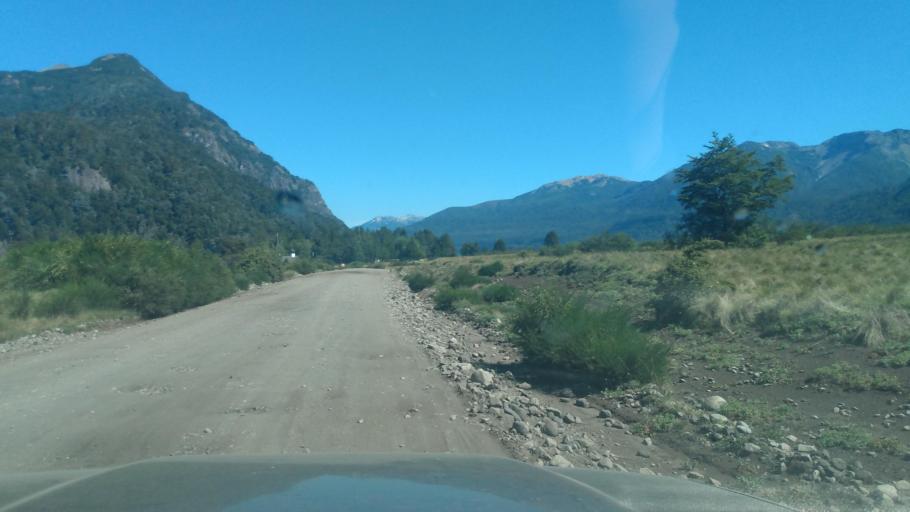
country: AR
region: Neuquen
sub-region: Departamento de Lacar
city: San Martin de los Andes
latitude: -39.7455
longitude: -71.5203
